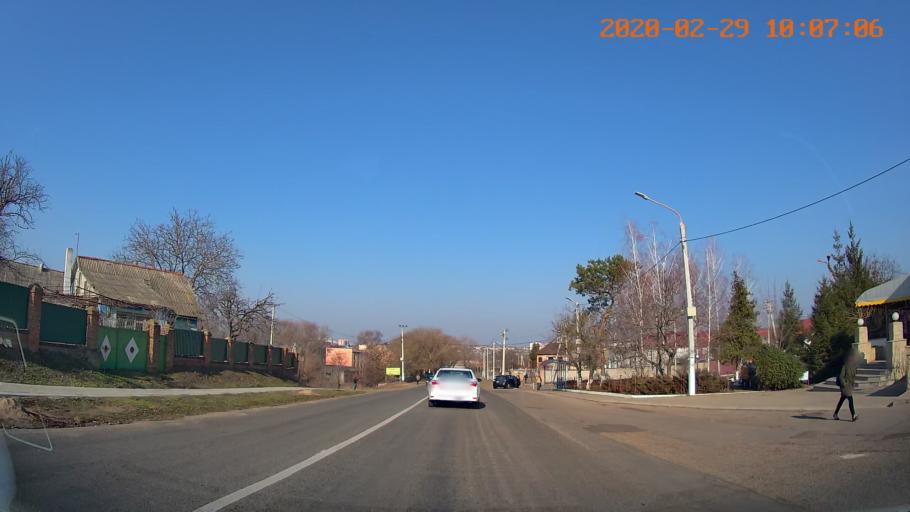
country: MD
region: Telenesti
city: Tiraspolul Nou
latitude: 46.8192
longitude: 29.6673
